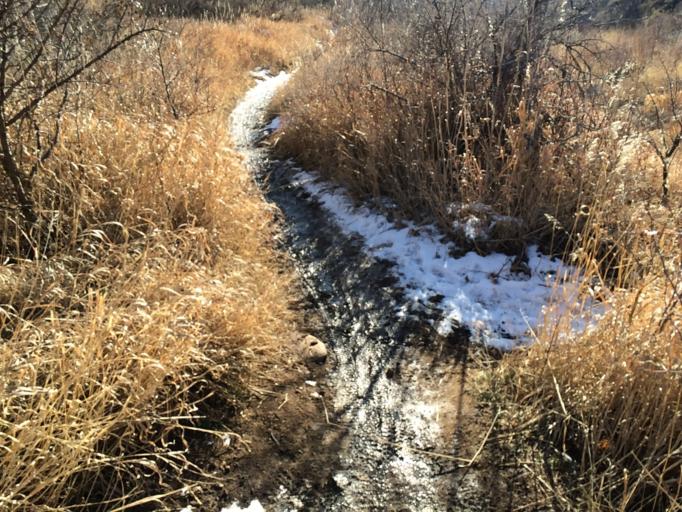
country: US
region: Colorado
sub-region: Boulder County
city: Boulder
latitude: 39.9203
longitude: -105.2595
